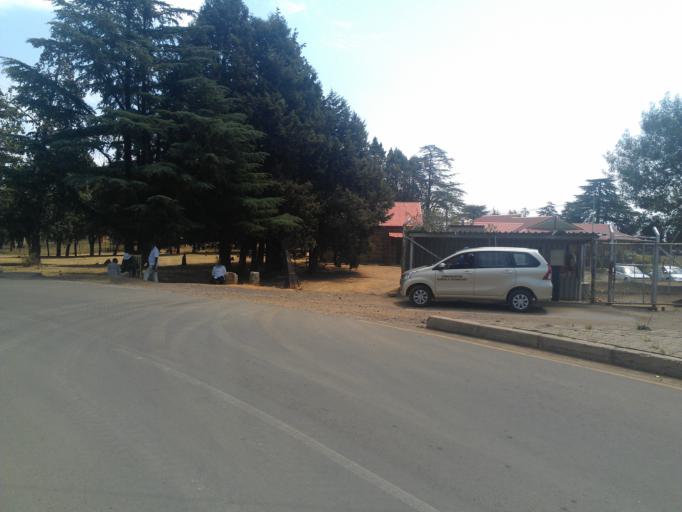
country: LS
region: Berea
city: Teyateyaneng
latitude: -29.1446
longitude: 27.7401
